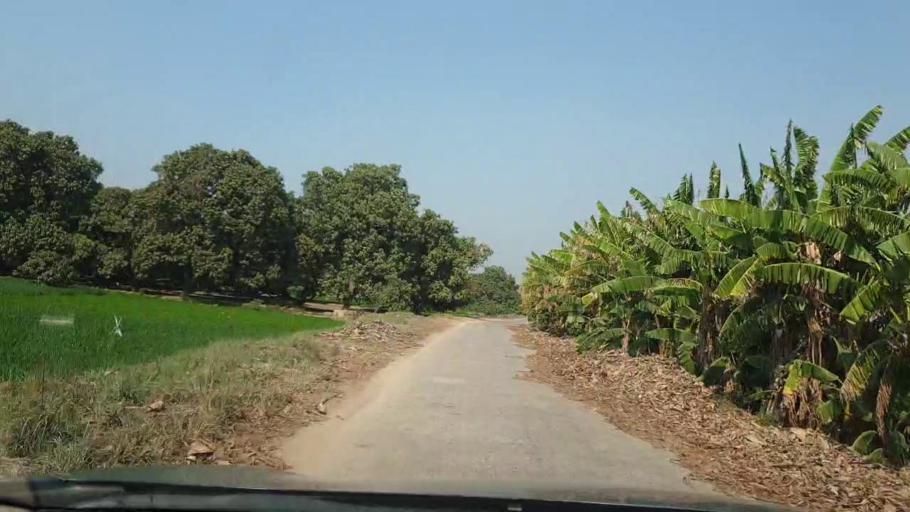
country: PK
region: Sindh
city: Tando Allahyar
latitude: 25.4846
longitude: 68.7915
